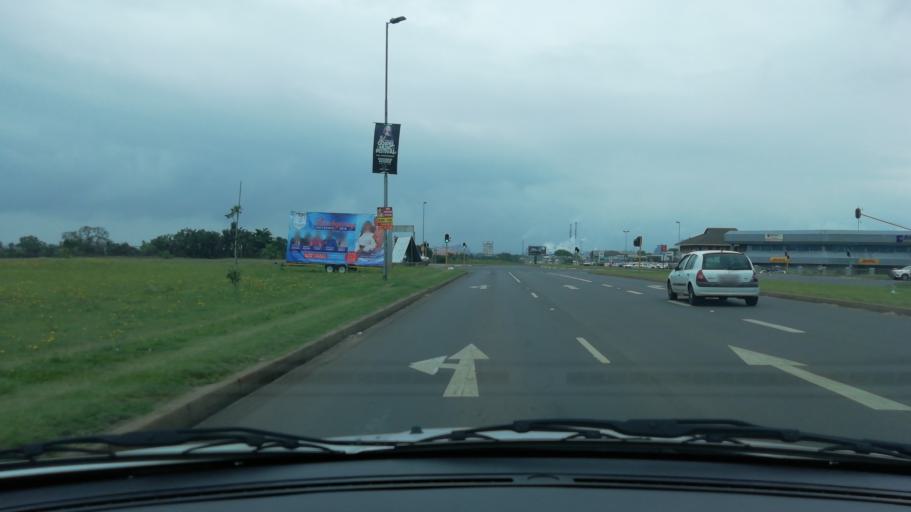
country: ZA
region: KwaZulu-Natal
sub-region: uThungulu District Municipality
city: Richards Bay
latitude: -28.7567
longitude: 32.0454
